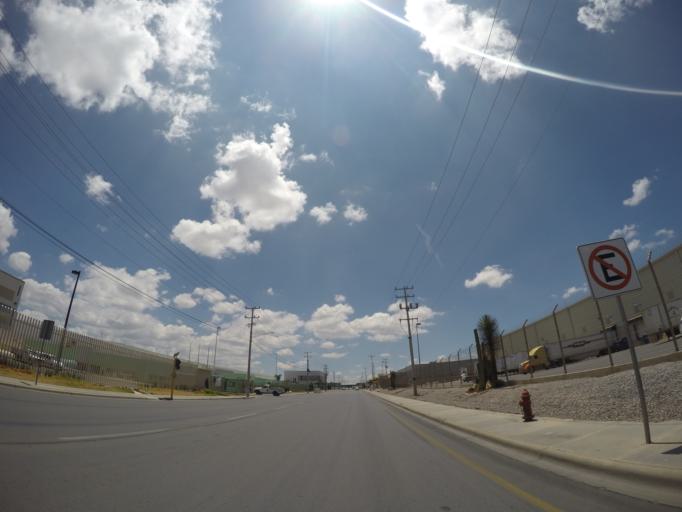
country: MX
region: San Luis Potosi
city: La Pila
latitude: 22.0394
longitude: -100.8918
